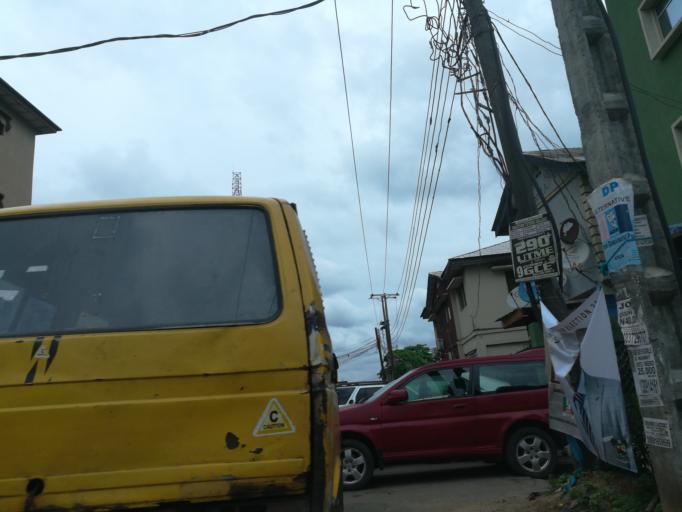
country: NG
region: Lagos
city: Ebute Metta
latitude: 6.4856
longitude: 3.3878
